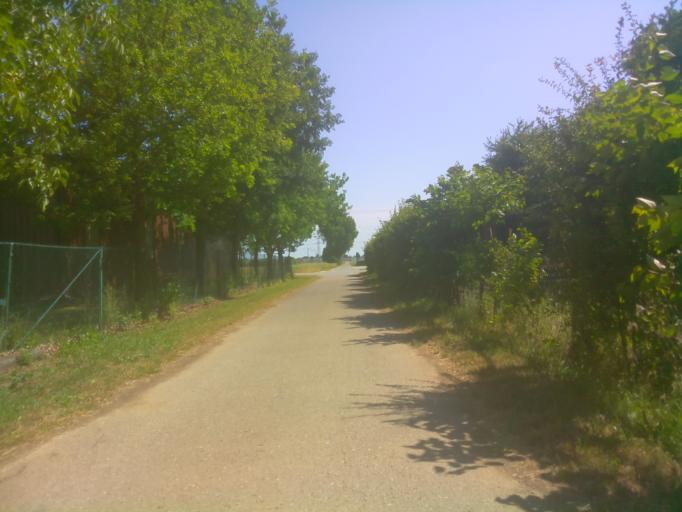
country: DE
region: Baden-Wuerttemberg
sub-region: Karlsruhe Region
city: Heddesheim
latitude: 49.5208
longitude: 8.5986
